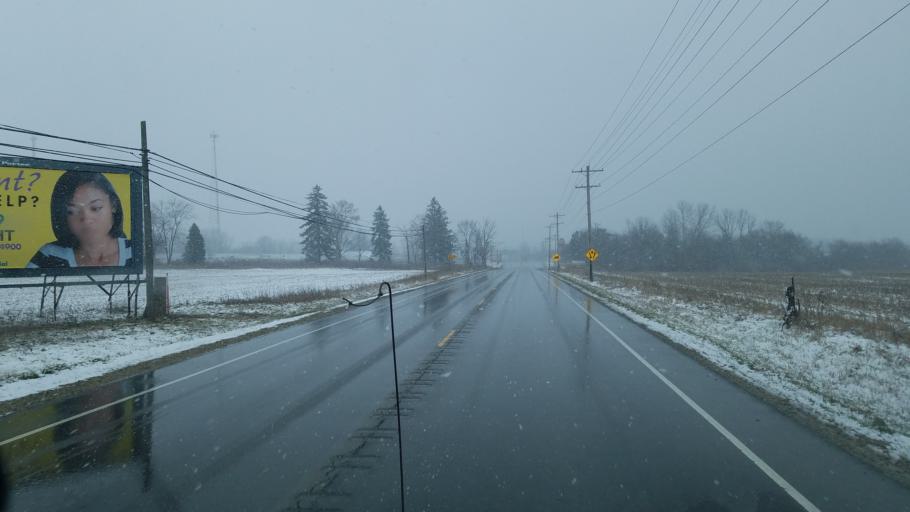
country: US
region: Indiana
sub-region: Wayne County
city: Richmond
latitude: 39.8743
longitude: -84.9360
